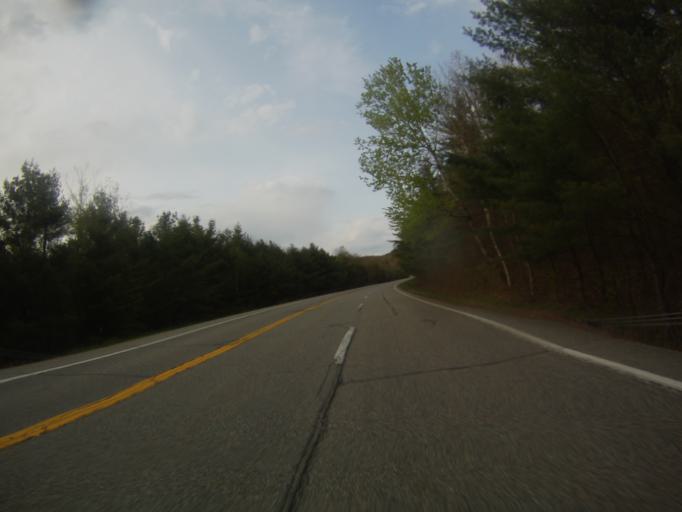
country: US
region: New York
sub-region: Essex County
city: Ticonderoga
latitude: 43.7351
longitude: -73.5979
